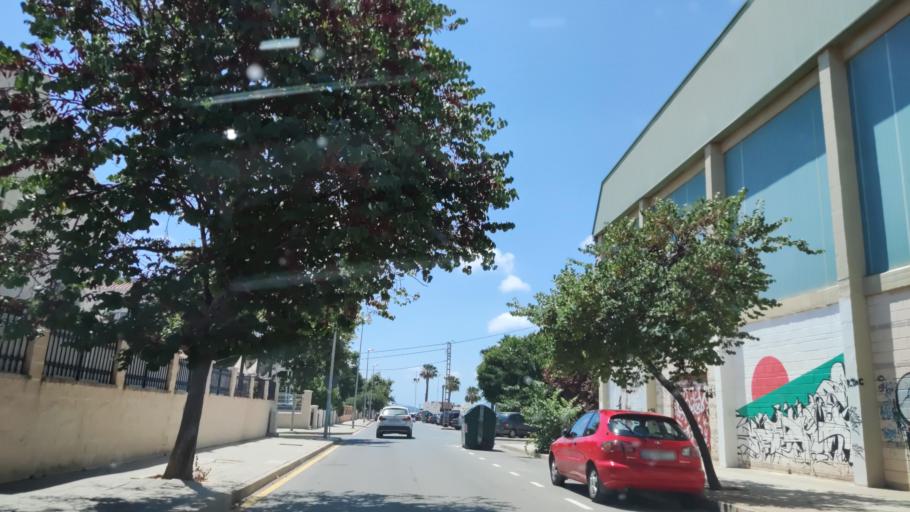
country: ES
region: Murcia
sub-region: Murcia
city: Los Alcazares
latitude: 37.7545
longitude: -0.8378
